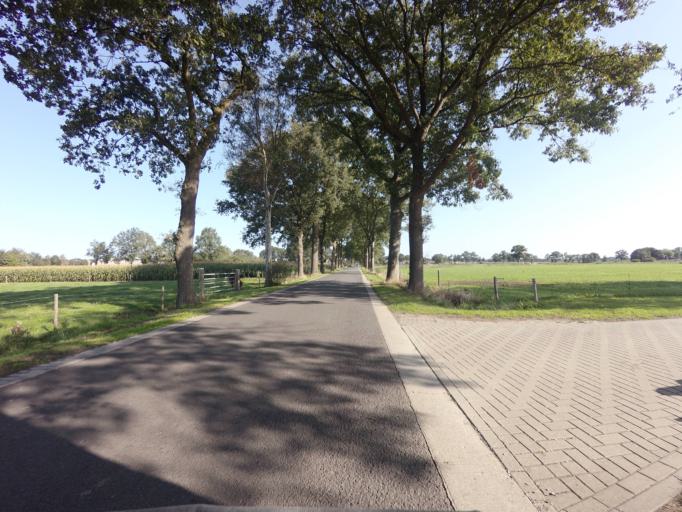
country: NL
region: Overijssel
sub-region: Gemeente Raalte
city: Raalte
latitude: 52.4149
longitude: 6.2870
